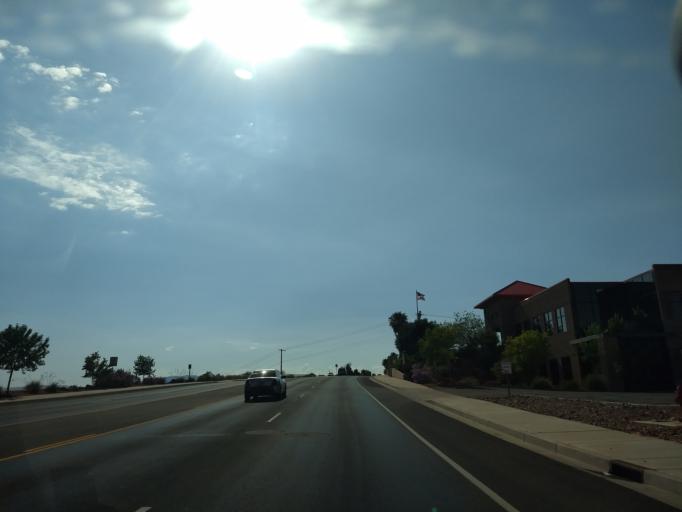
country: US
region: Utah
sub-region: Washington County
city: Saint George
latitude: 37.1123
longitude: -113.5655
